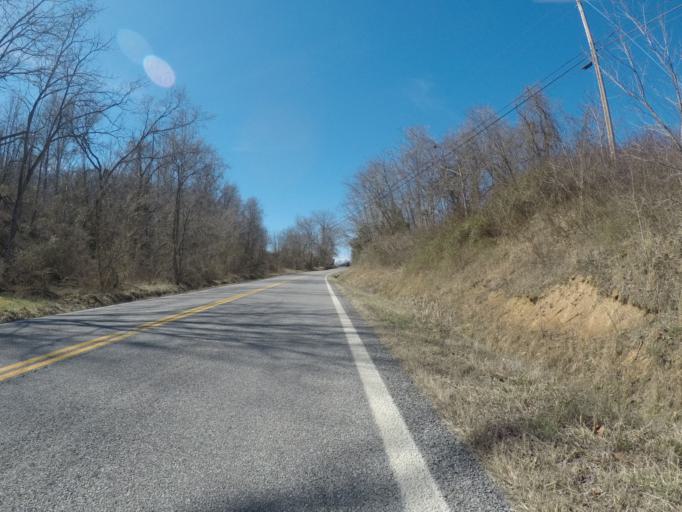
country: US
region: Ohio
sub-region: Lawrence County
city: Burlington
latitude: 38.4897
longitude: -82.5445
